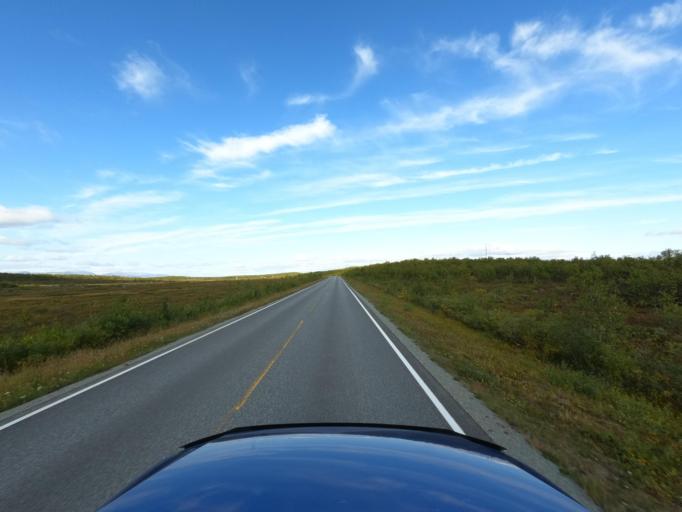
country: NO
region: Finnmark Fylke
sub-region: Karasjok
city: Karasjohka
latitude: 69.6971
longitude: 25.2573
